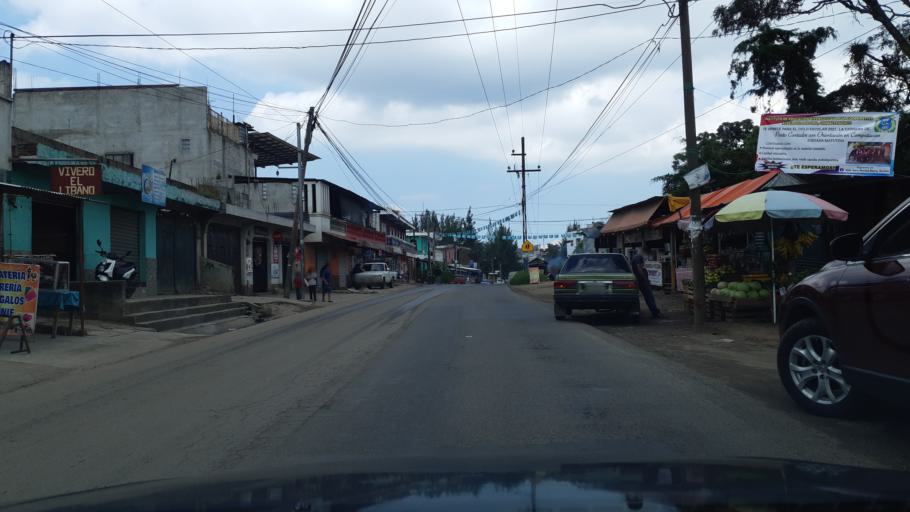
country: GT
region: Chimaltenango
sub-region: Municipio de Chimaltenango
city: Chimaltenango
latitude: 14.6774
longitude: -90.8007
